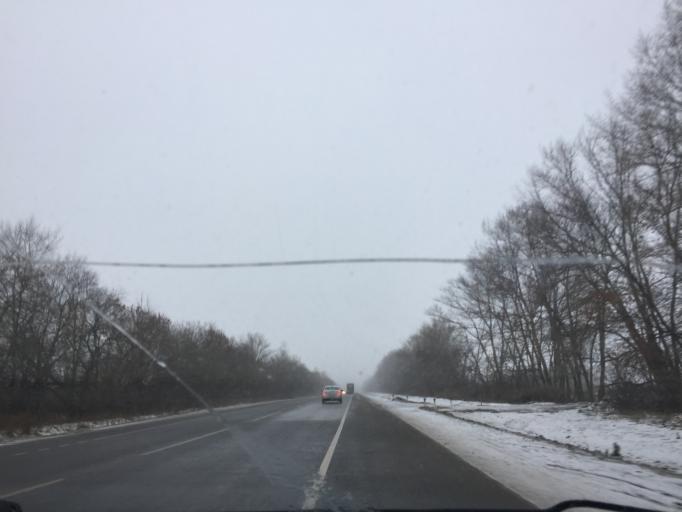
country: RU
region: Tula
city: Plavsk
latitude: 53.8020
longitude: 37.3811
